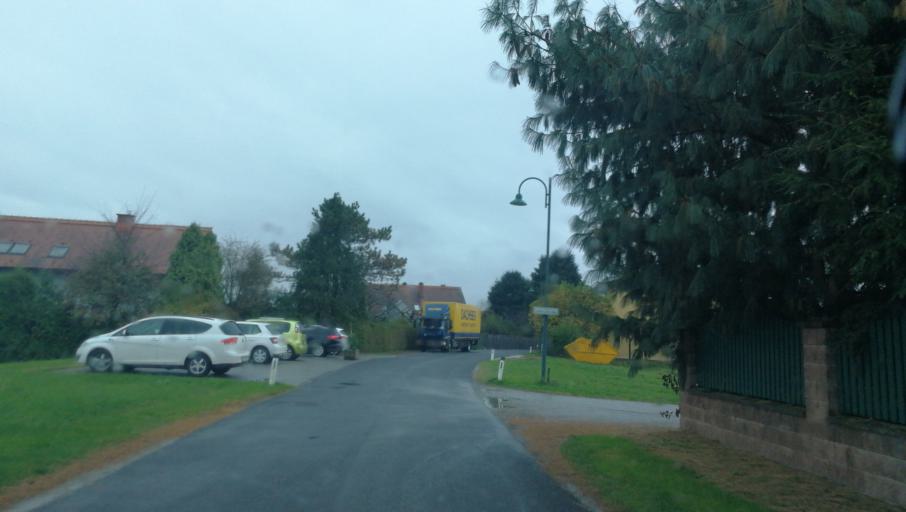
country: AT
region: Styria
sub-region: Politischer Bezirk Leibnitz
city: Sankt Veit am Vogau
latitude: 46.7338
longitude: 15.6218
